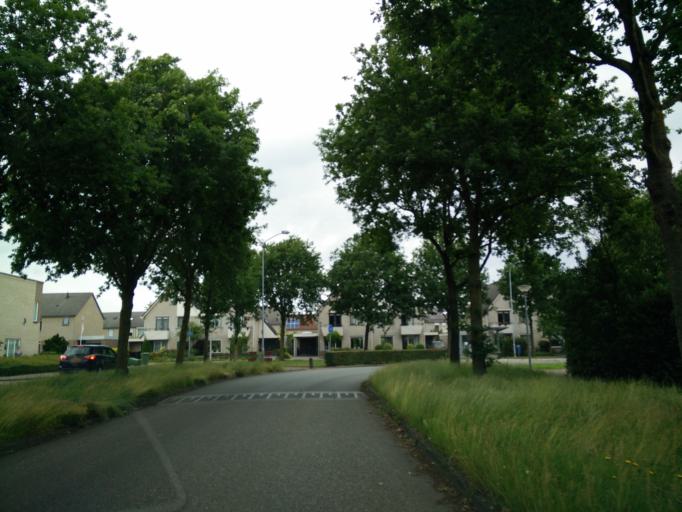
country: NL
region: Drenthe
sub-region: Gemeente Assen
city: Assen
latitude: 53.0198
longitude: 6.5953
